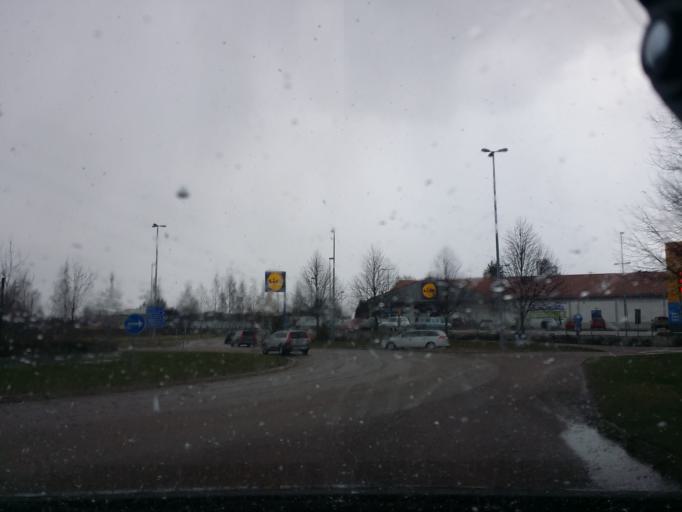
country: SE
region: Vaestmanland
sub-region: Sala Kommun
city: Sala
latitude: 59.9161
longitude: 16.6154
